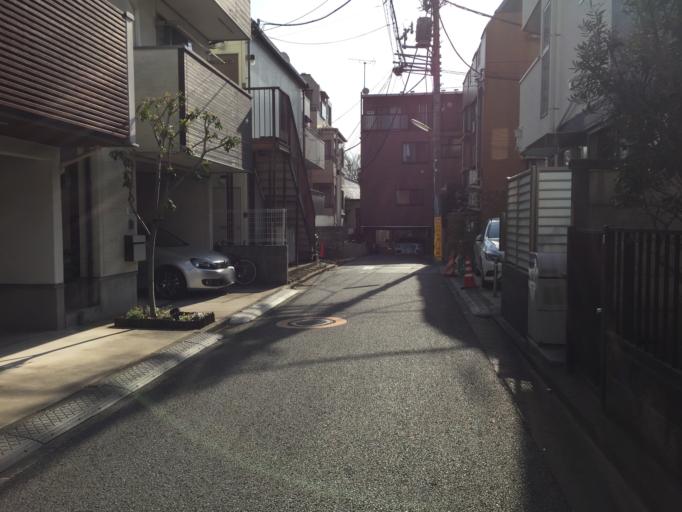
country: JP
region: Tokyo
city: Tokyo
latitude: 35.6408
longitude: 139.6730
